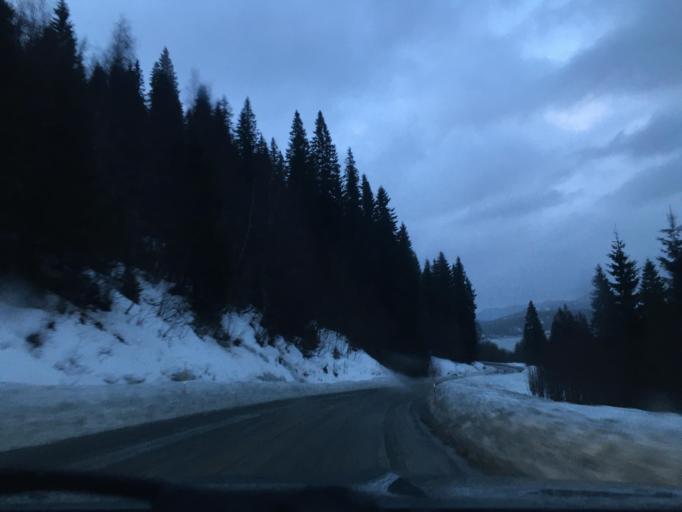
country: NO
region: Nordland
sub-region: Rana
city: Hauknes
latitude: 66.2881
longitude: 13.9082
